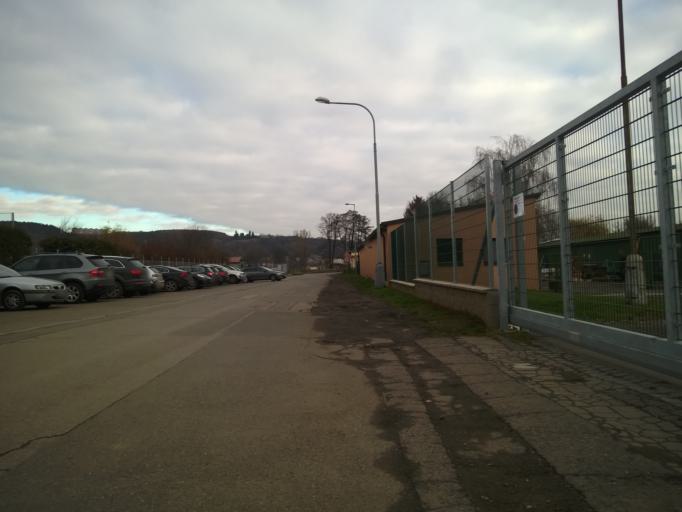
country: CZ
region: Praha
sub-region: Praha 1
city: Mala Strana
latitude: 50.1103
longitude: 14.4099
